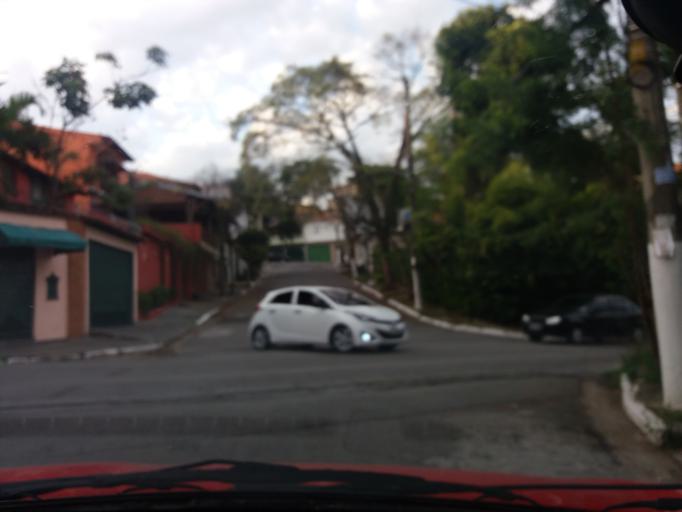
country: BR
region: Sao Paulo
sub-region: Taboao Da Serra
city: Taboao da Serra
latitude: -23.5941
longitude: -46.7464
